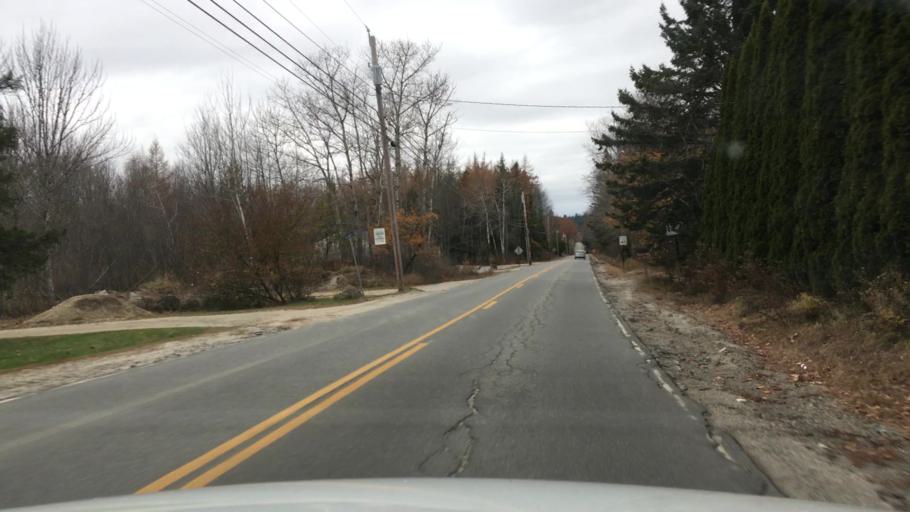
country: US
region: Maine
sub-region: Hancock County
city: Sedgwick
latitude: 44.4147
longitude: -68.6083
